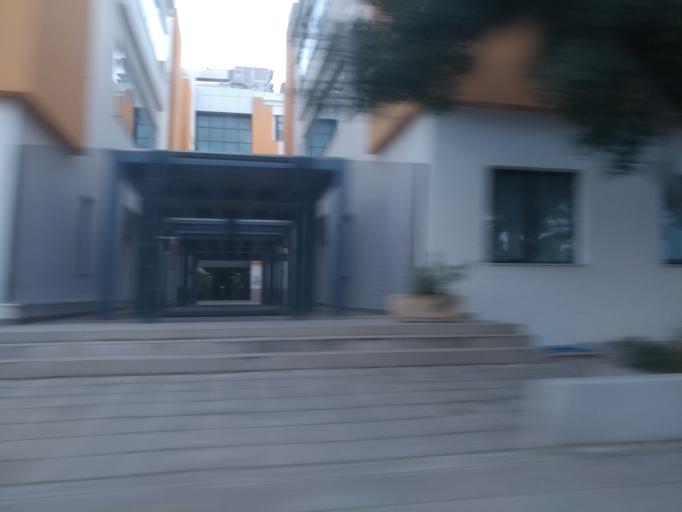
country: CY
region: Pafos
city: Paphos
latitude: 34.7742
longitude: 32.4283
